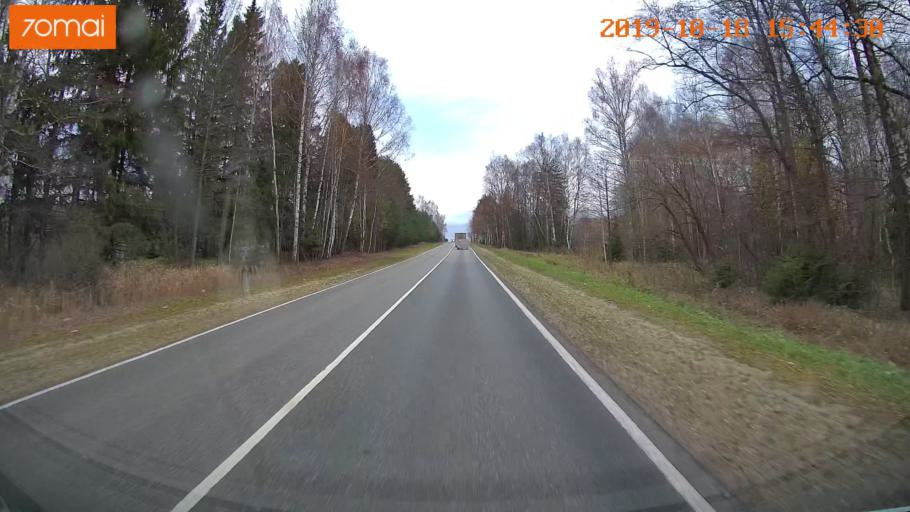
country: RU
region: Vladimir
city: Golovino
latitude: 55.9822
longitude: 40.5509
